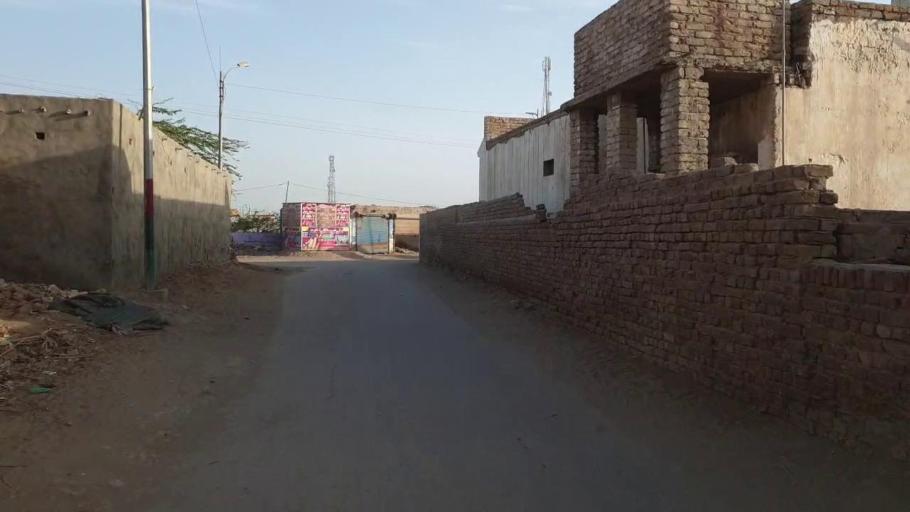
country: PK
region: Sindh
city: Jam Sahib
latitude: 26.2978
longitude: 68.6312
